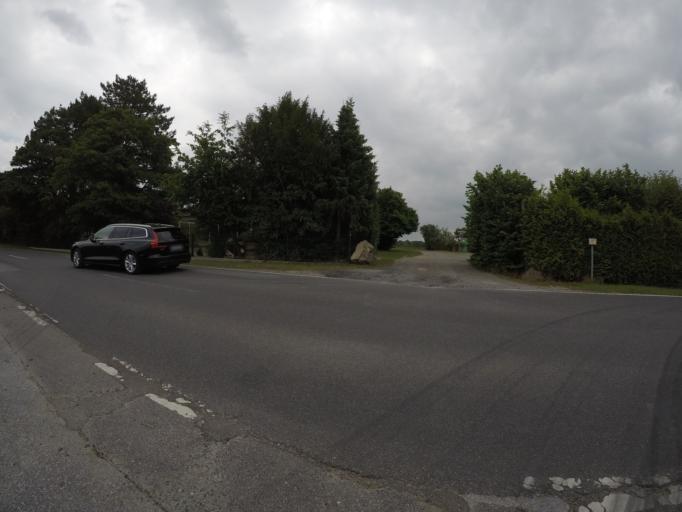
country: DE
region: North Rhine-Westphalia
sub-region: Regierungsbezirk Dusseldorf
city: Wesel
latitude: 51.7281
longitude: 6.6706
